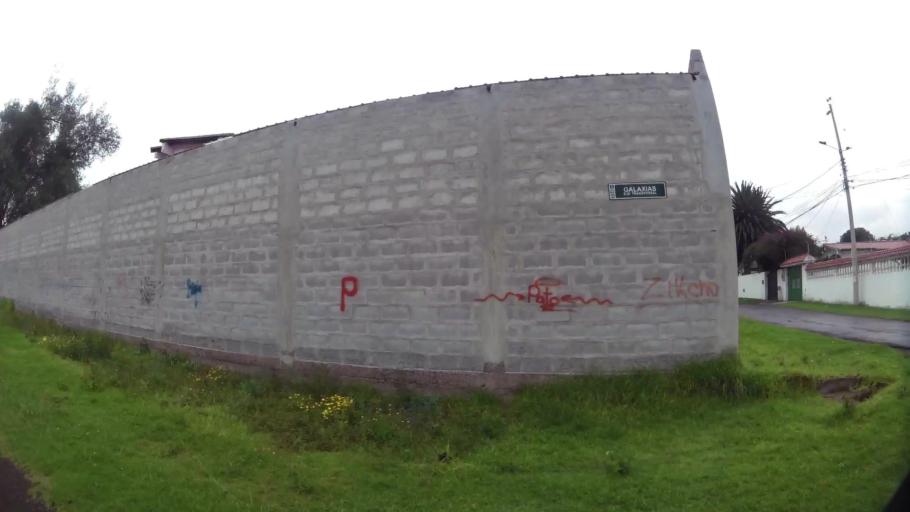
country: EC
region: Pichincha
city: Sangolqui
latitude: -0.2842
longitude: -78.4508
